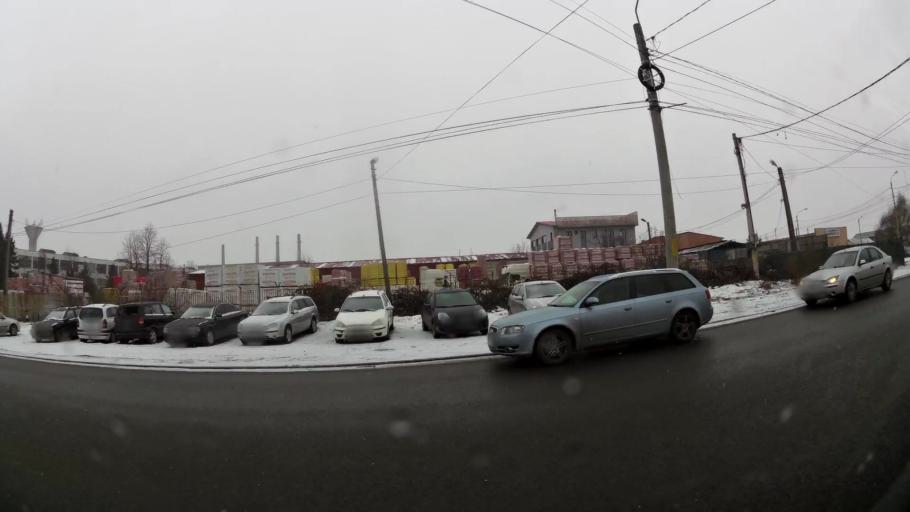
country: RO
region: Dambovita
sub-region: Municipiul Targoviste
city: Targoviste
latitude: 44.9285
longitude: 25.4329
